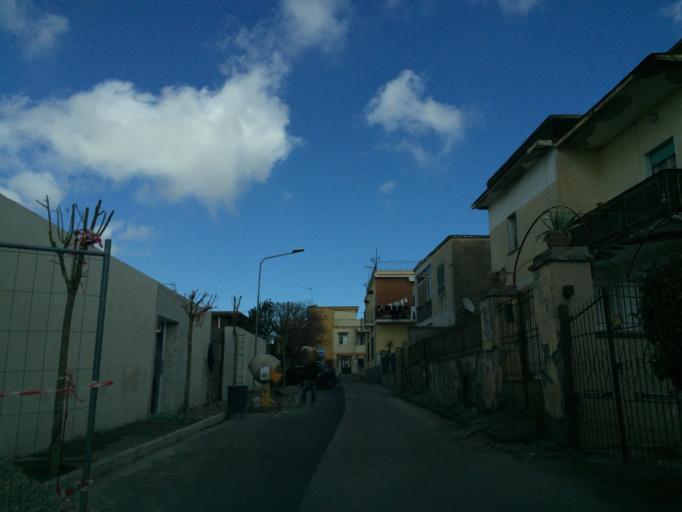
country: IT
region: Campania
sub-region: Provincia di Napoli
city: Massa di Somma
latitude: 40.8442
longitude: 14.3734
